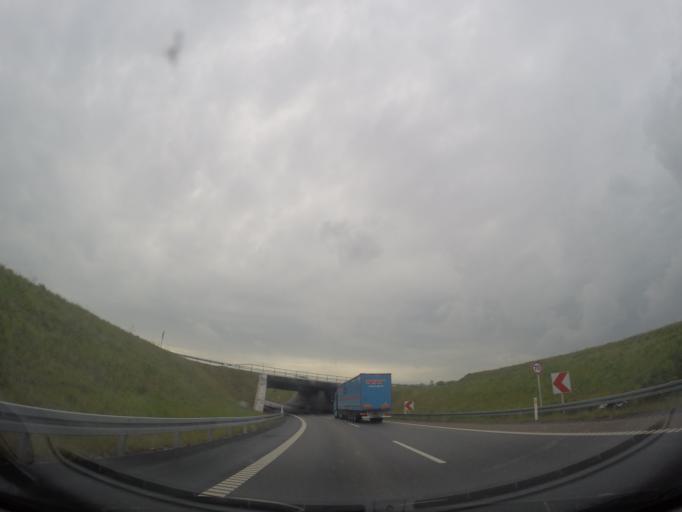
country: DK
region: Capital Region
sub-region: Ballerup Kommune
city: Ballerup
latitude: 55.7042
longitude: 12.3689
